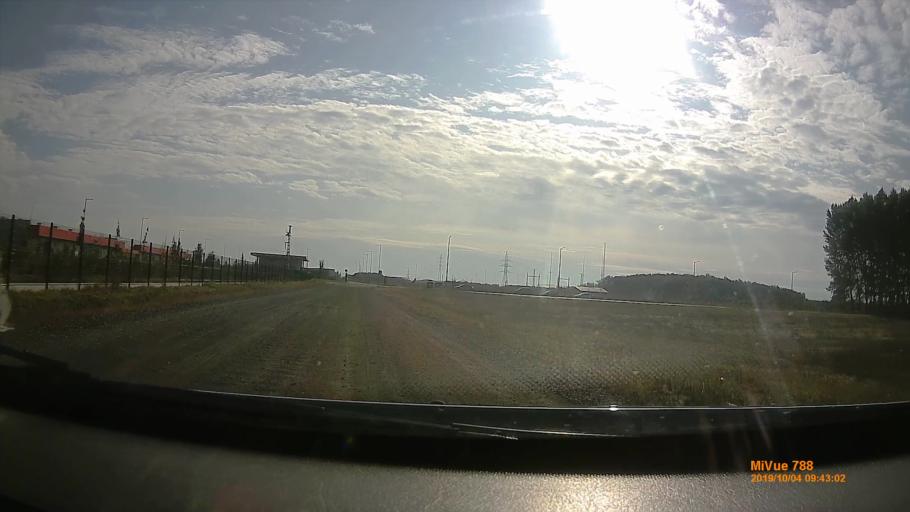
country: HU
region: Szabolcs-Szatmar-Bereg
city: Nyirtelek
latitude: 47.9475
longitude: 21.6455
